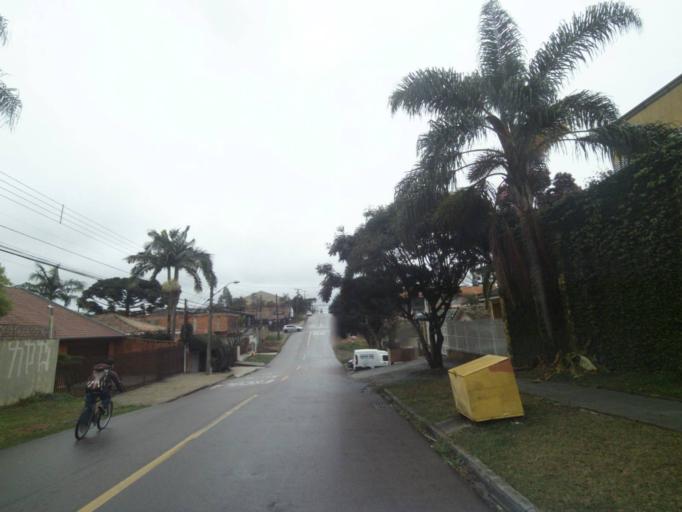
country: BR
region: Parana
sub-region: Curitiba
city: Curitiba
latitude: -25.5143
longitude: -49.3008
